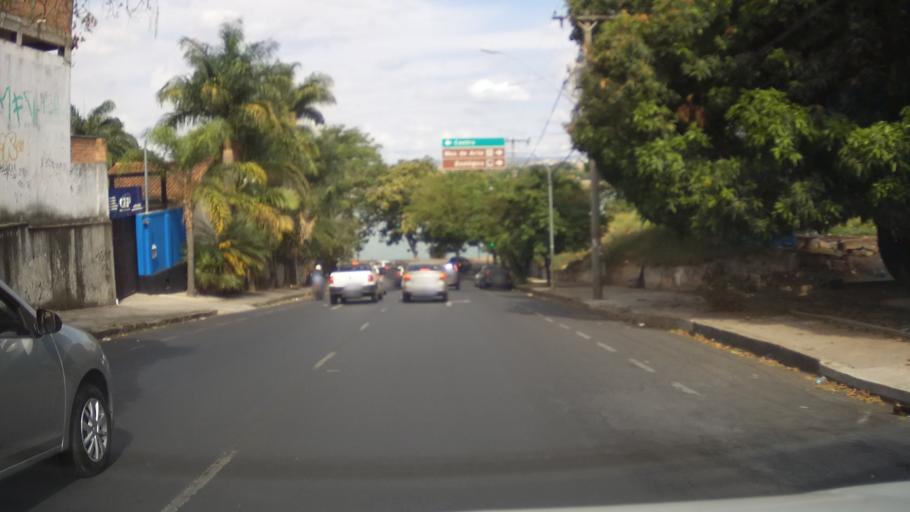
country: BR
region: Minas Gerais
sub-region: Belo Horizonte
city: Belo Horizonte
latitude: -19.8439
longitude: -43.9718
